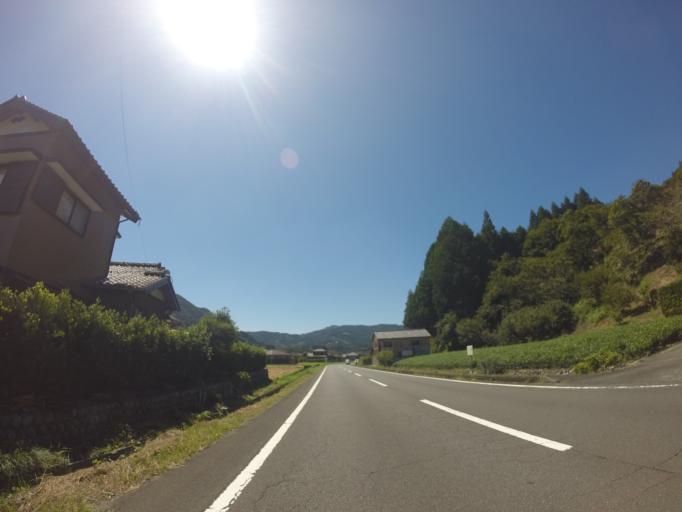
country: JP
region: Shizuoka
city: Fujieda
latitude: 34.9183
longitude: 138.2051
